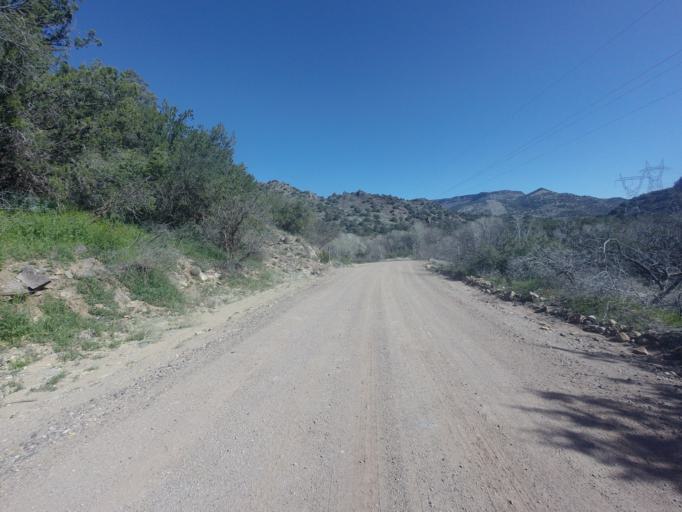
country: US
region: Arizona
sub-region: Gila County
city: Pine
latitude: 34.3851
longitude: -111.6599
